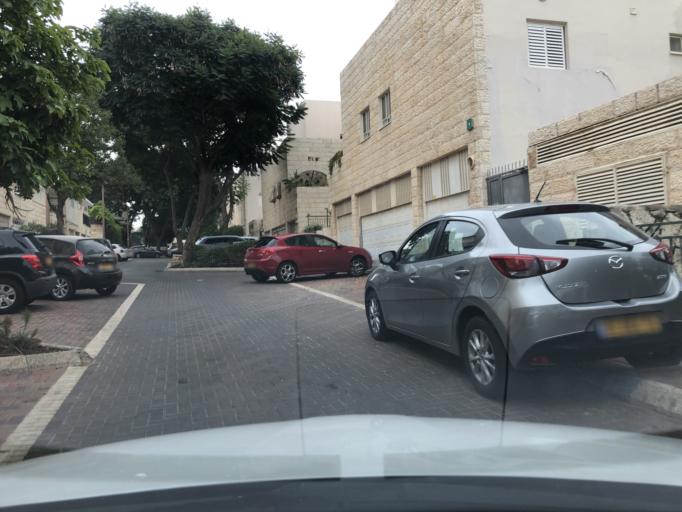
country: IL
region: Central District
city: Modiin
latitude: 31.9045
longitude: 35.0097
